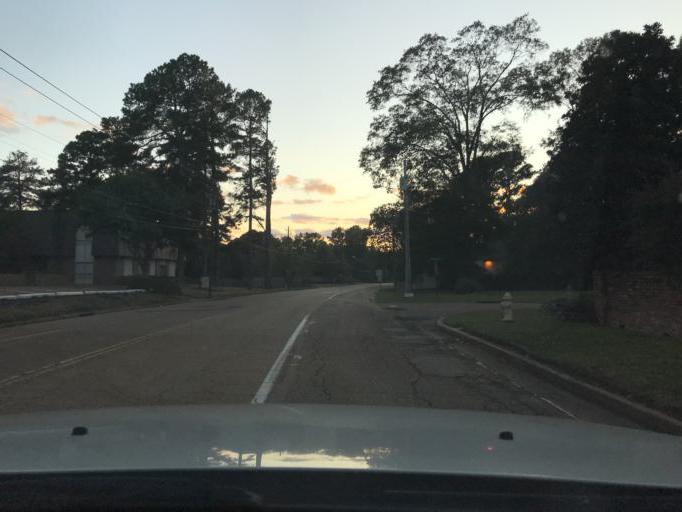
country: US
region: Mississippi
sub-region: Rankin County
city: Flowood
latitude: 32.3465
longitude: -90.1587
